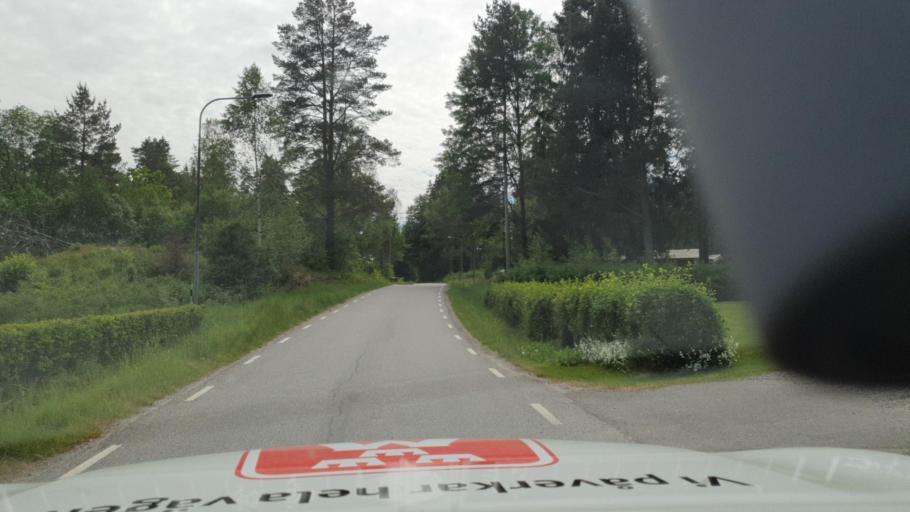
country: SE
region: Vaestra Goetaland
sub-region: Vanersborgs Kommun
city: Vargon
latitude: 58.2706
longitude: 12.5060
